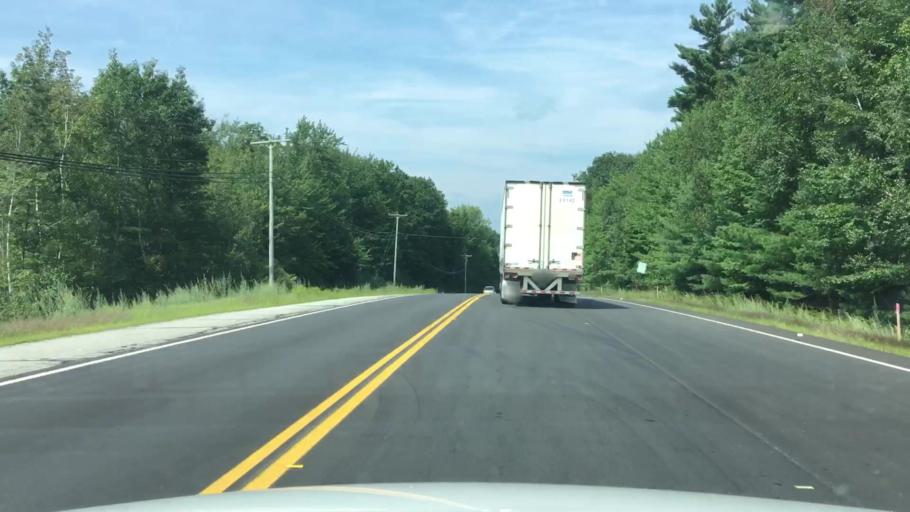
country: US
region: Maine
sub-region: Androscoggin County
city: Turner
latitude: 44.2629
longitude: -70.2635
